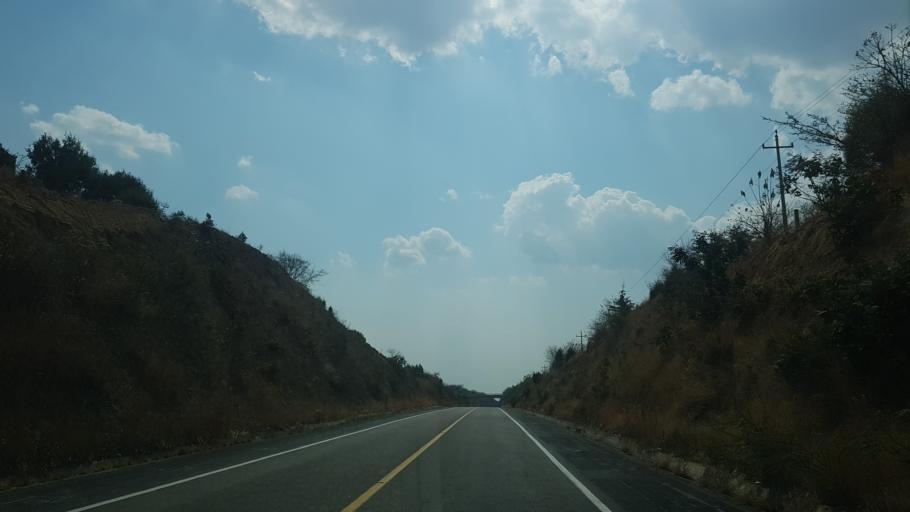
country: MX
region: Puebla
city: San Juan Amecac
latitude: 18.8161
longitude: -98.6665
